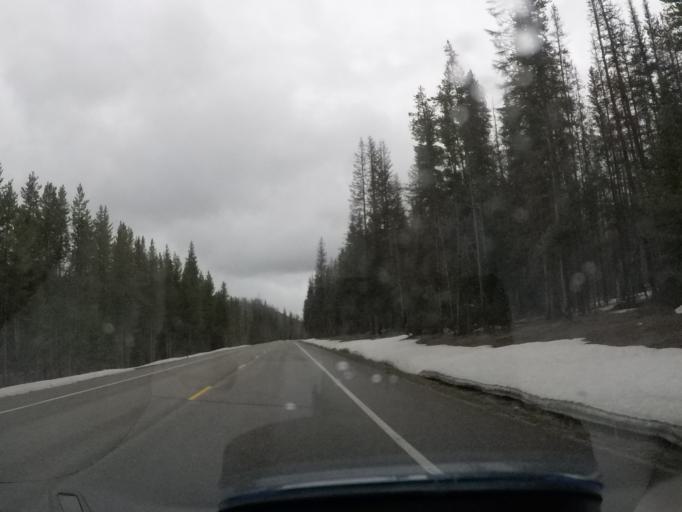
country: US
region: Idaho
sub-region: Teton County
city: Driggs
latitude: 44.0379
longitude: -110.6933
